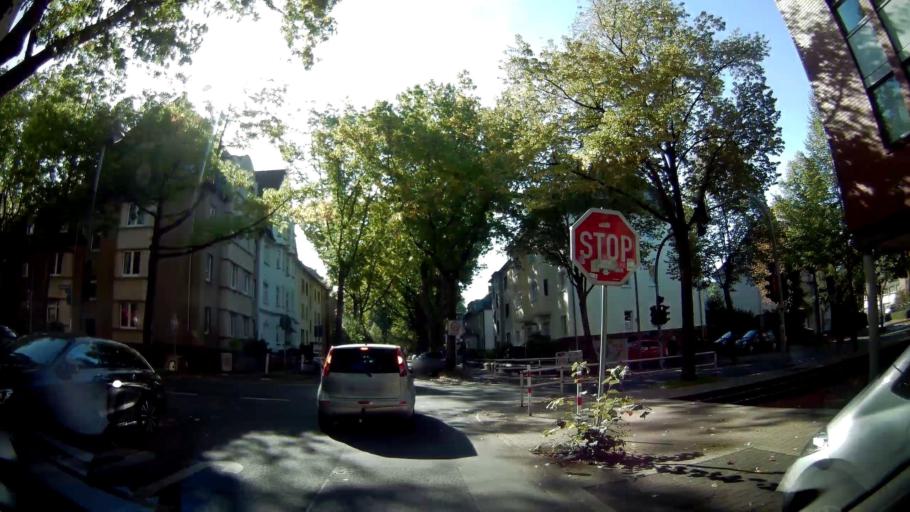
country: DE
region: North Rhine-Westphalia
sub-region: Regierungsbezirk Arnsberg
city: Bochum
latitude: 51.4686
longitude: 7.2135
